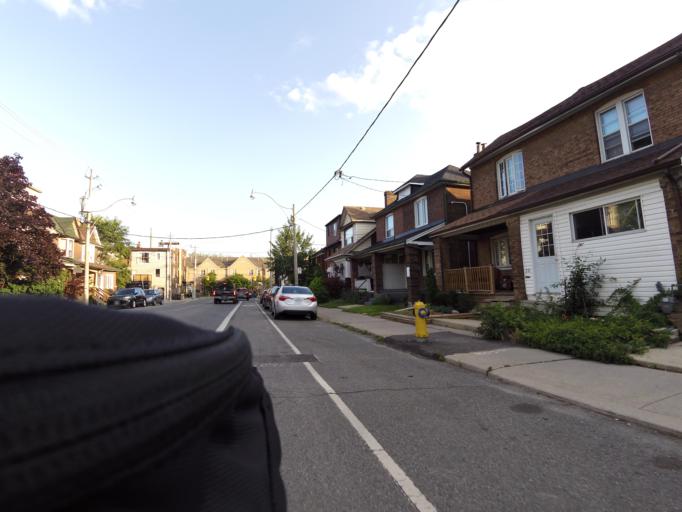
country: CA
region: Ontario
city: Toronto
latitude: 43.6652
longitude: -79.3257
